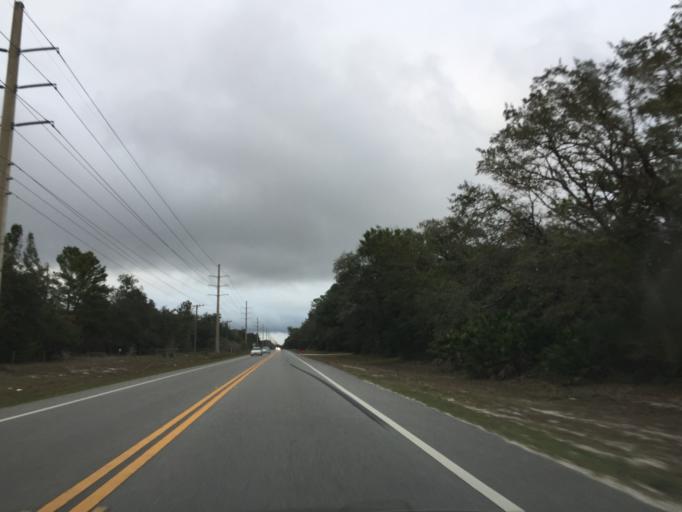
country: US
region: Florida
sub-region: Seminole County
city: Chuluota
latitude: 28.6172
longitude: -81.1295
